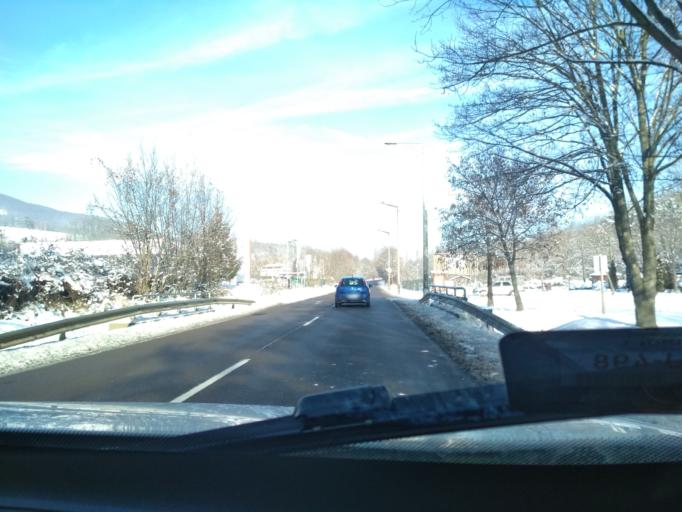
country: HU
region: Nograd
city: Somoskoujfalu
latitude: 48.1346
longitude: 19.8144
